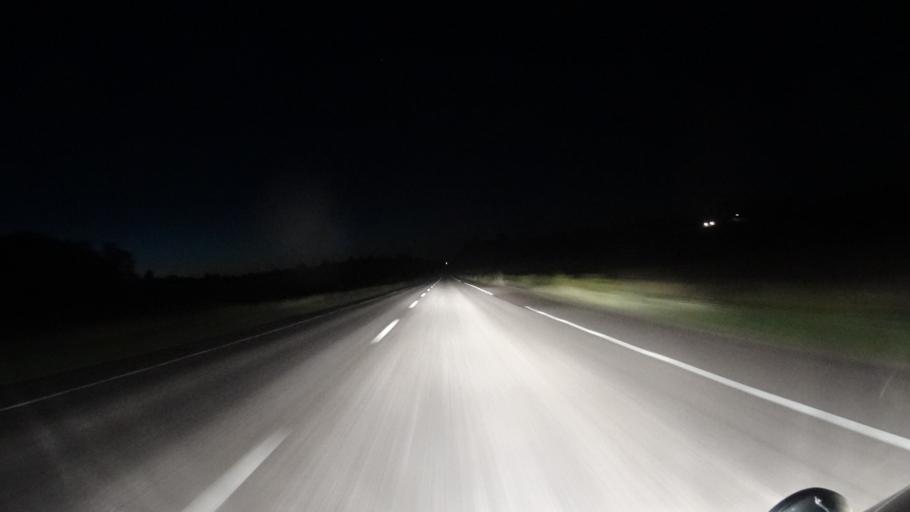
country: SE
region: OEstergoetland
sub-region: Odeshogs Kommun
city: OEdeshoeg
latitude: 58.2522
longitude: 14.7291
